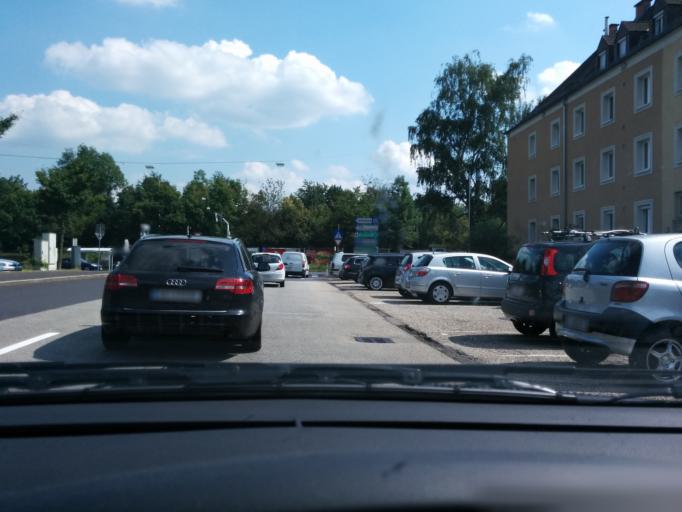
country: AT
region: Upper Austria
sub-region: Linz Stadt
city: Linz
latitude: 48.3238
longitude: 14.2953
